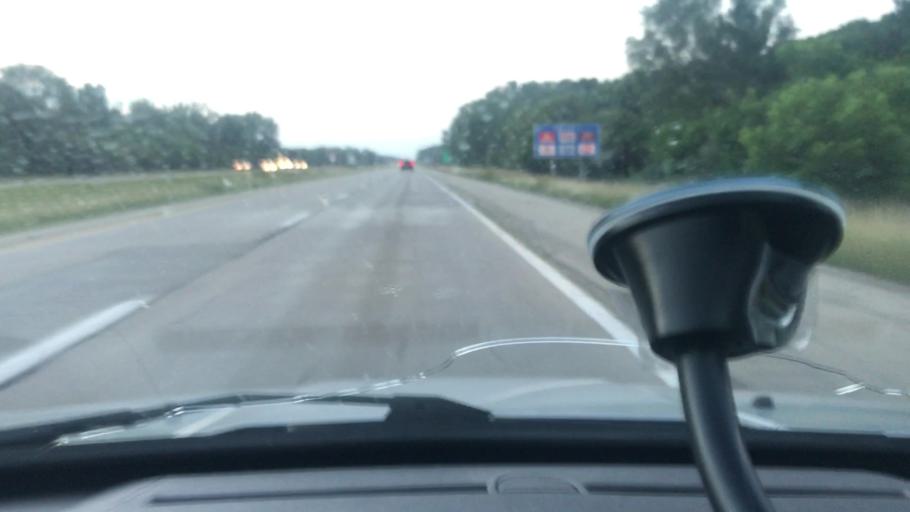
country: US
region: Illinois
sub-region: Peoria County
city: Bellevue
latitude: 40.7569
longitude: -89.6707
